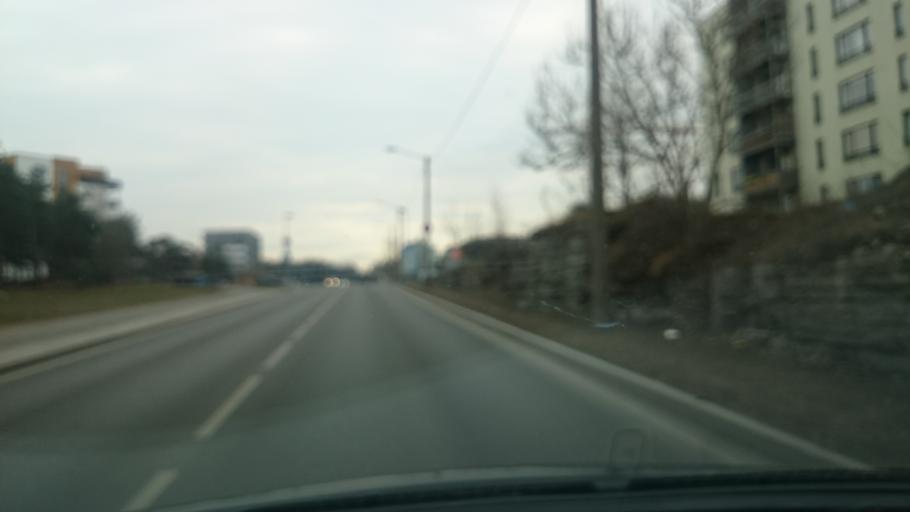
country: EE
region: Harju
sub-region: Saue vald
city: Laagri
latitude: 59.3977
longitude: 24.6452
